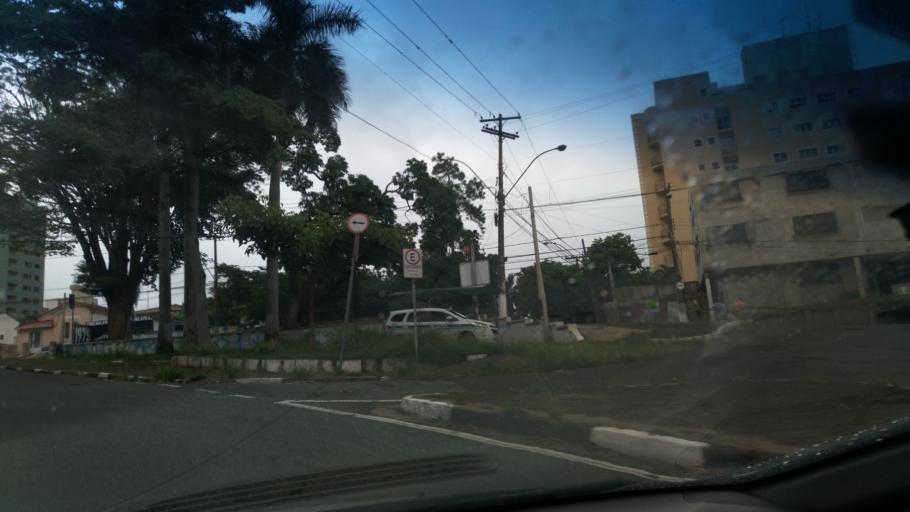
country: BR
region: Sao Paulo
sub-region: Campinas
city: Campinas
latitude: -22.9122
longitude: -47.0500
